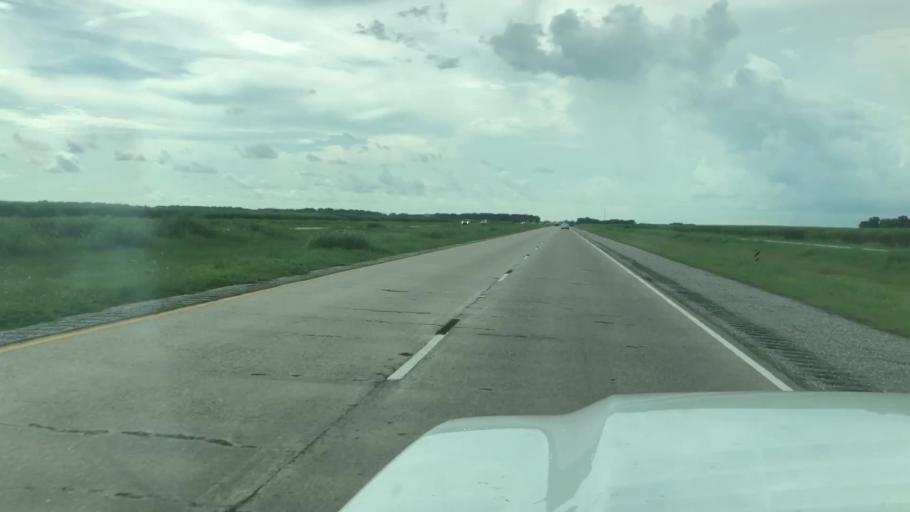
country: US
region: Louisiana
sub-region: Saint Mary Parish
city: Baldwin
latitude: 29.8476
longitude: -91.5904
